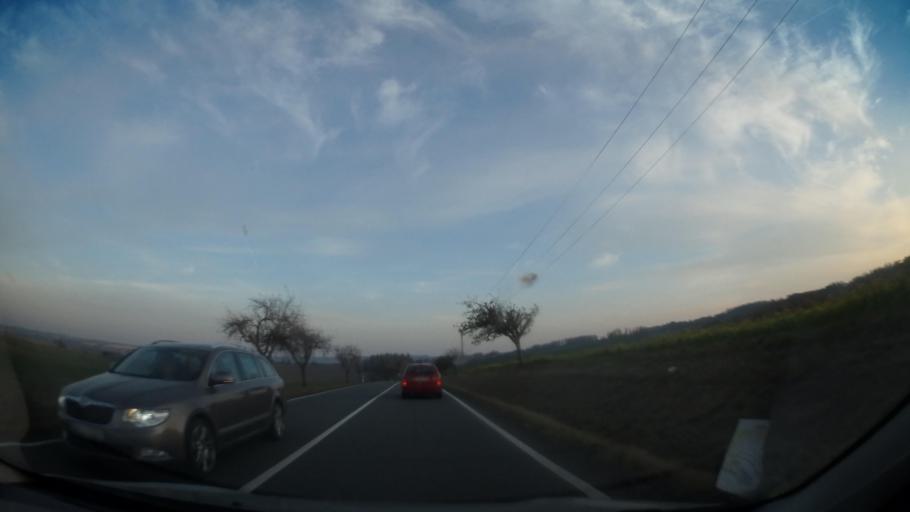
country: CZ
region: Central Bohemia
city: Cechtice
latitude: 49.6344
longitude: 15.0294
